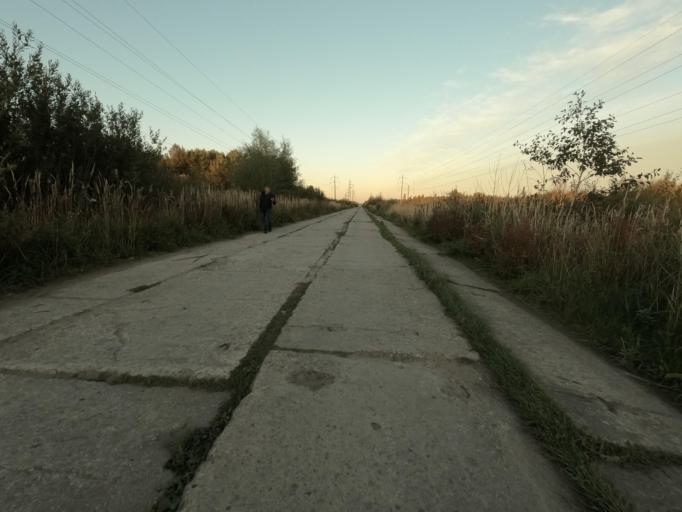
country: RU
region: Leningrad
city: Otradnoye
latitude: 59.7587
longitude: 30.7796
